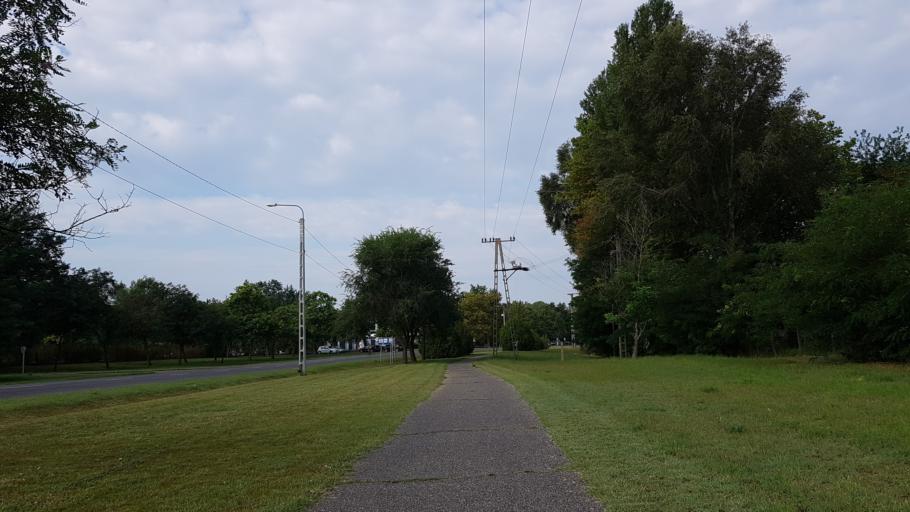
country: HU
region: Bacs-Kiskun
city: Lakitelek
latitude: 46.8623
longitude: 19.9936
